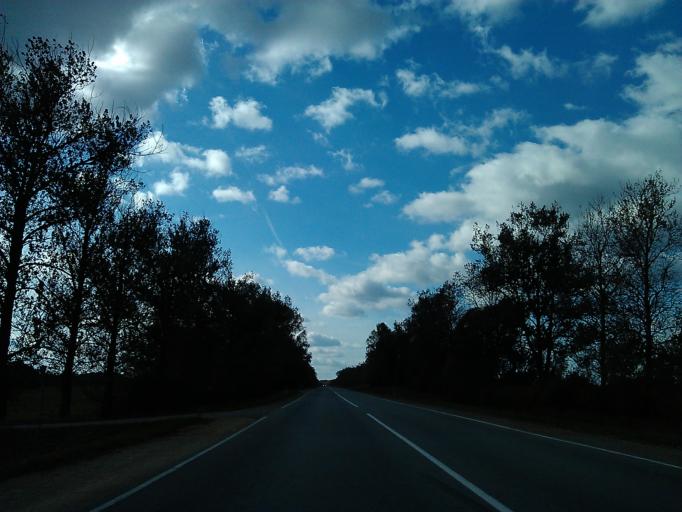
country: LV
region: Jekabpils Rajons
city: Jekabpils
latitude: 56.4783
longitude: 25.9823
